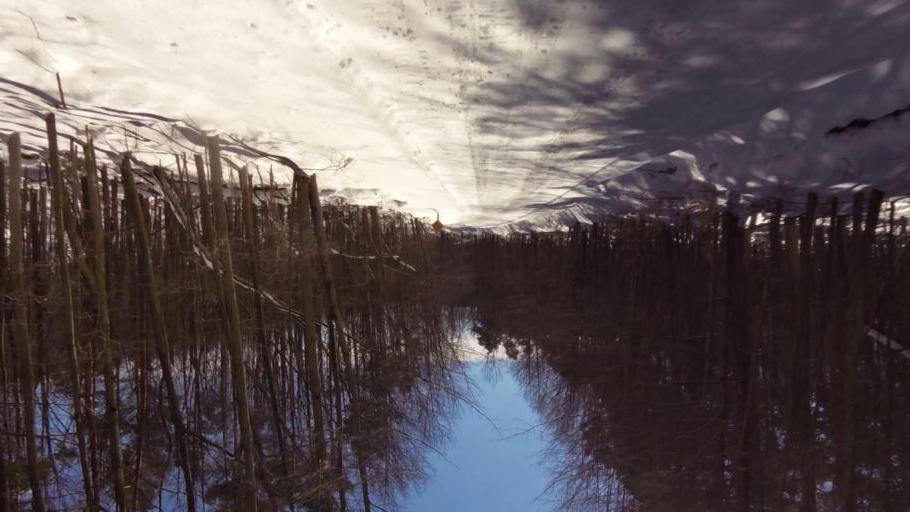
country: US
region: New York
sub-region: Allegany County
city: Houghton
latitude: 42.3306
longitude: -78.2039
